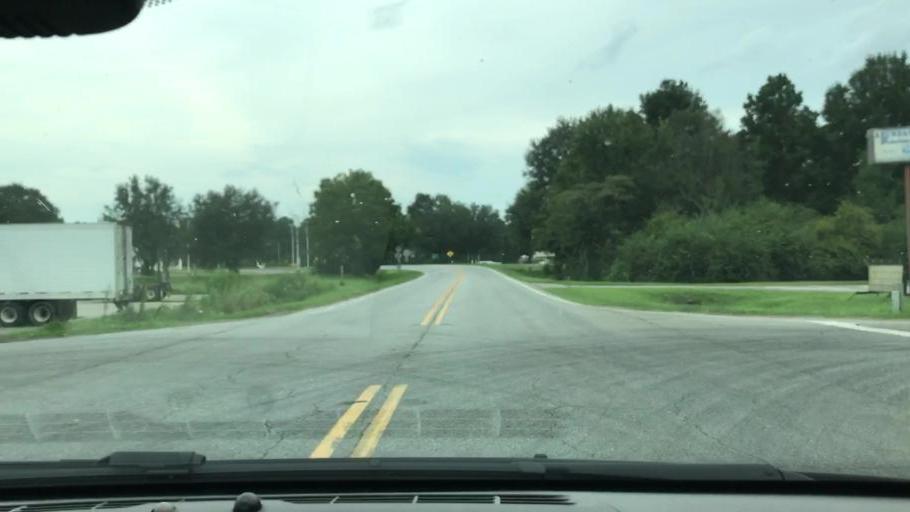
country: US
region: Georgia
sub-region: Early County
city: Blakely
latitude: 31.3713
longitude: -84.9578
